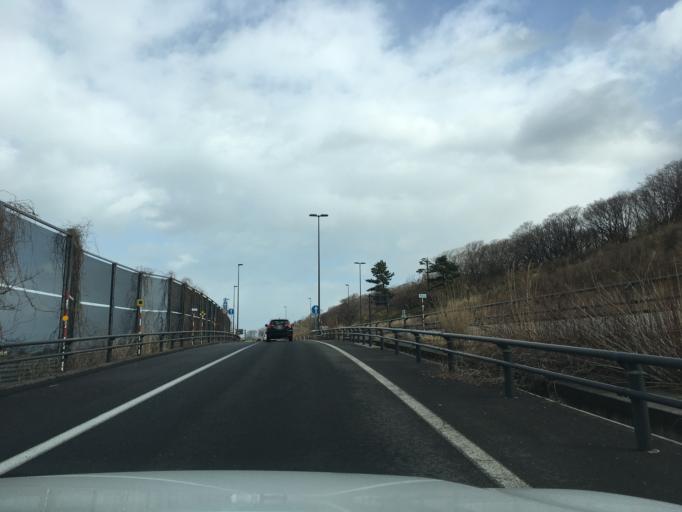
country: JP
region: Yamagata
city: Yuza
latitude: 39.2962
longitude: 139.9765
